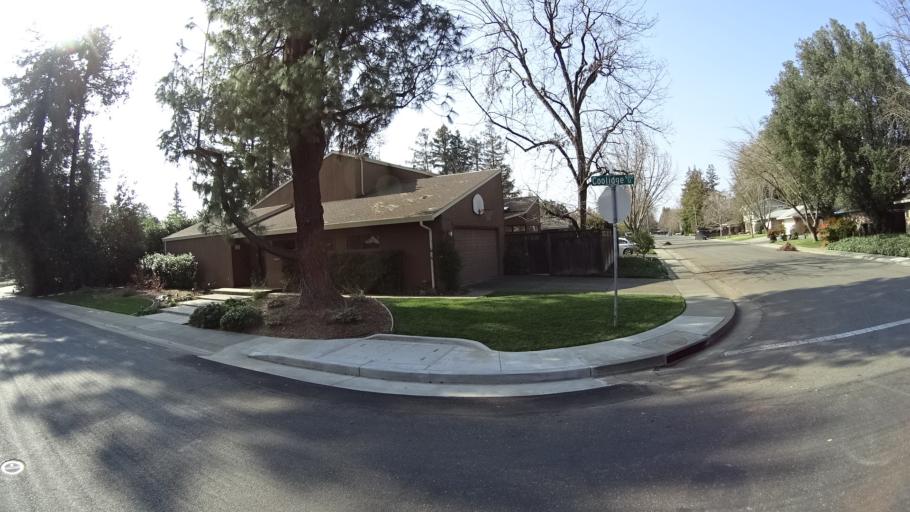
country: US
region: California
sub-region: Yolo County
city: Davis
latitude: 38.5497
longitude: -121.7748
